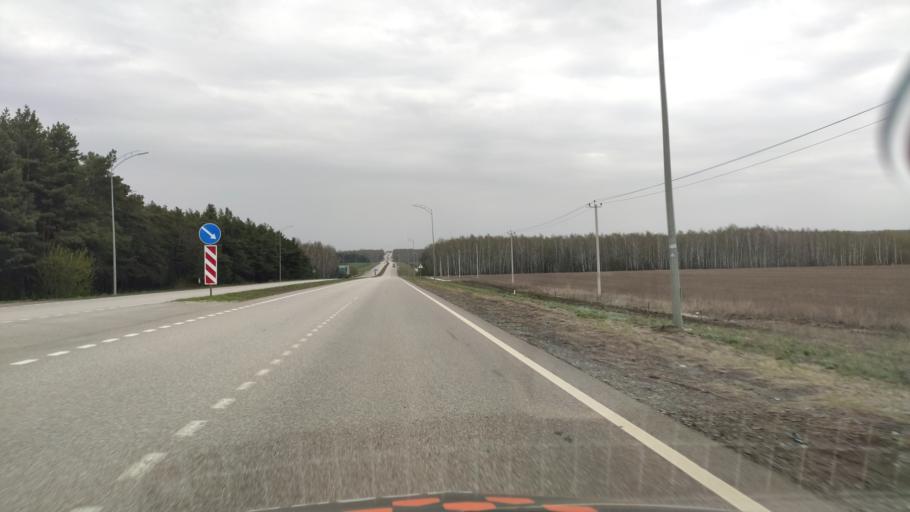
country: RU
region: Belgorod
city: Staryy Oskol
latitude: 51.3992
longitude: 37.8742
